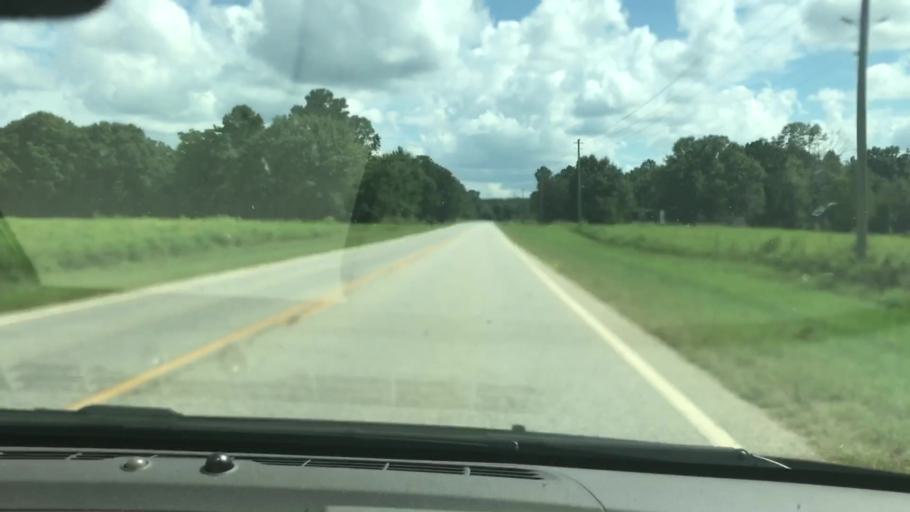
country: US
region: Georgia
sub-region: Clay County
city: Fort Gaines
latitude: 31.6509
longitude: -85.0466
